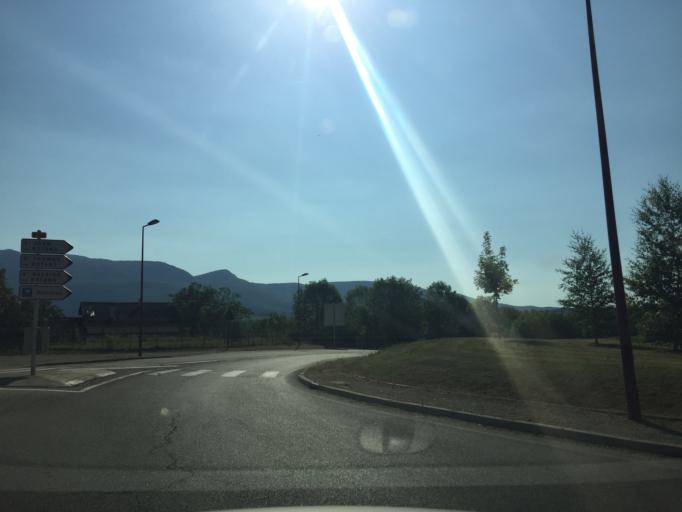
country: FR
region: Rhone-Alpes
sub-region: Departement de la Drome
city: Saint-Laurent-en-Royans
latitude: 45.0281
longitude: 5.3221
